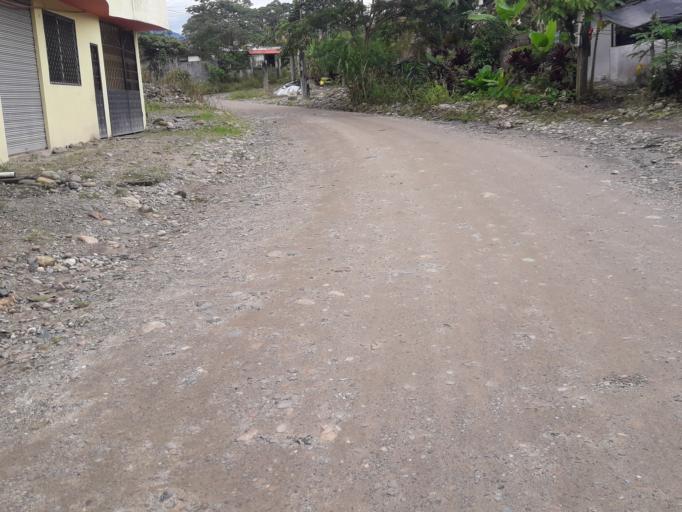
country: EC
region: Napo
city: Tena
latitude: -0.9836
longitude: -77.8226
